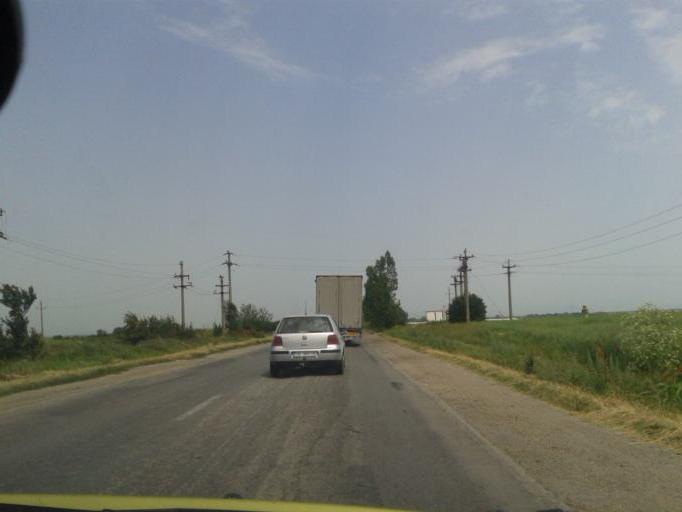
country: RO
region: Dambovita
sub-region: Oras Gaesti
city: Gaesti
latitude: 44.6916
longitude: 25.3127
